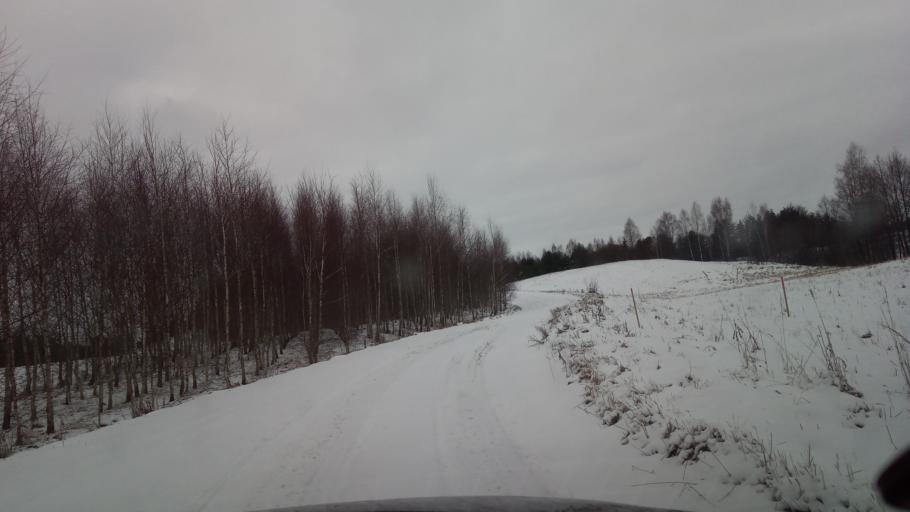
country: LT
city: Zarasai
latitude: 55.6829
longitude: 26.1064
